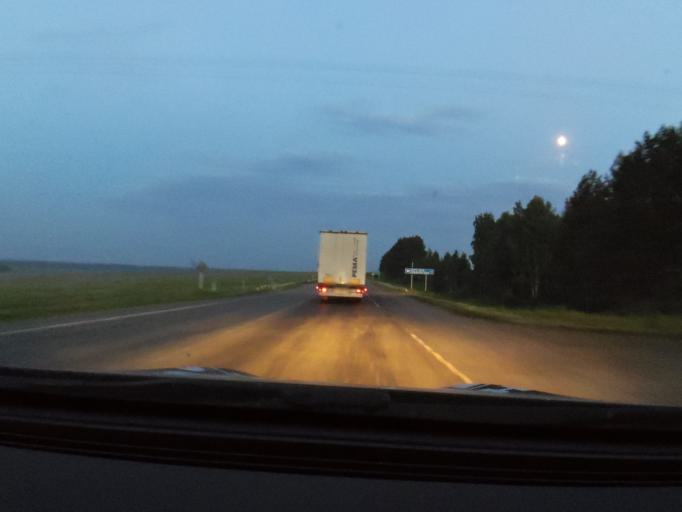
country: RU
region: Bashkortostan
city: Duvan
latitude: 56.0493
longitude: 58.1998
